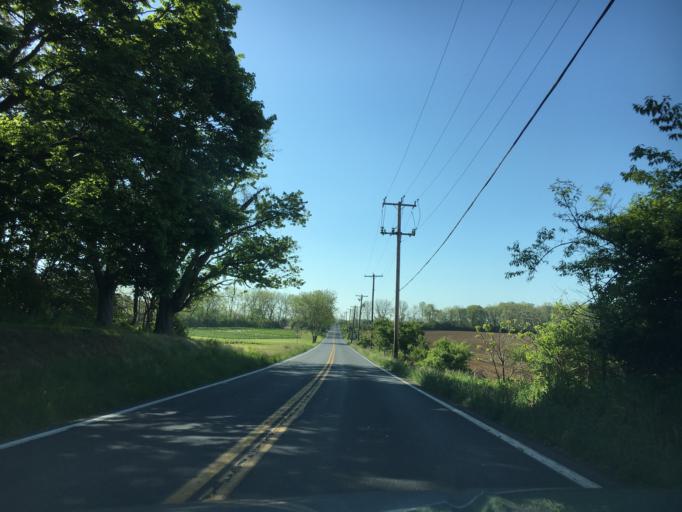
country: US
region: Pennsylvania
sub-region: Northampton County
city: North Catasauqua
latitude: 40.6833
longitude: -75.4445
